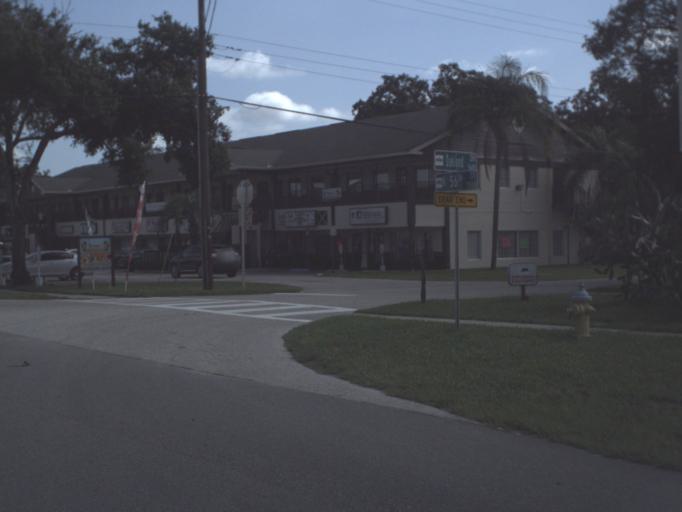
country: US
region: Florida
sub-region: Hillsborough County
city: Temple Terrace
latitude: 28.0170
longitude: -82.3933
